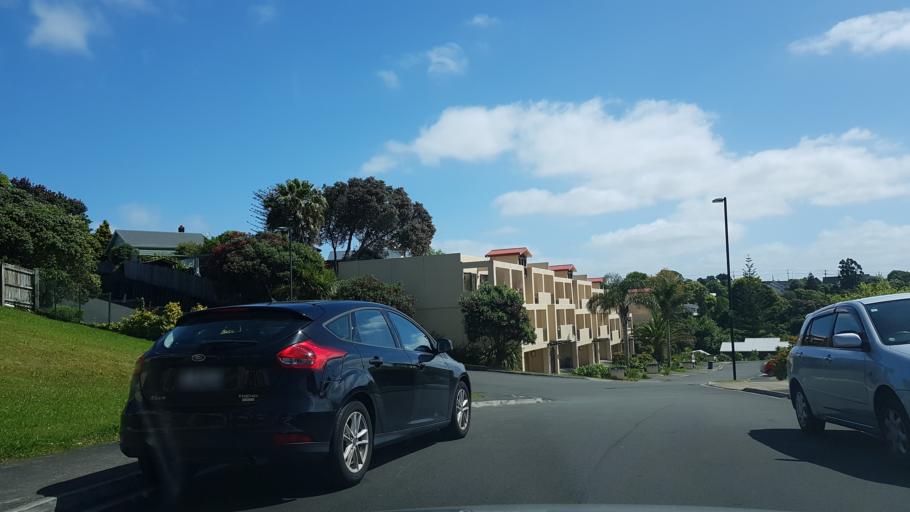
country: NZ
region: Auckland
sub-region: Auckland
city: North Shore
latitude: -36.8064
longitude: 174.7036
